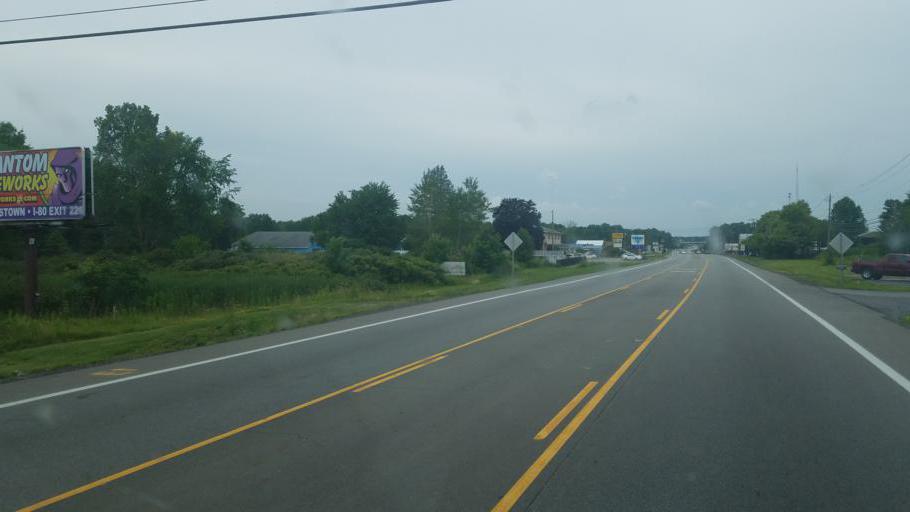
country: US
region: Ohio
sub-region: Trumbull County
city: Morgandale
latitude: 41.2870
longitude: -80.7664
